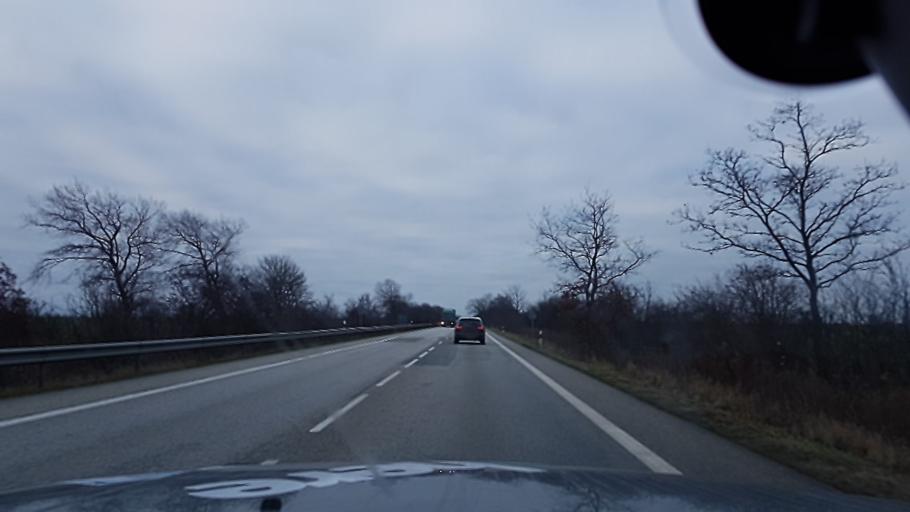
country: DE
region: Schleswig-Holstein
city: Fehmarn
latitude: 54.4762
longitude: 11.2078
